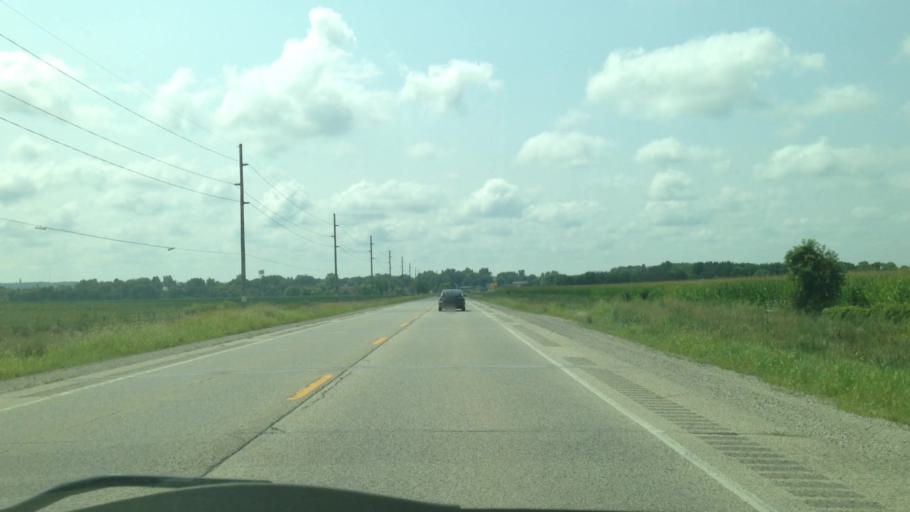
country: US
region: Iowa
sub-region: Benton County
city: Walford
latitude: 41.8121
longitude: -91.8723
